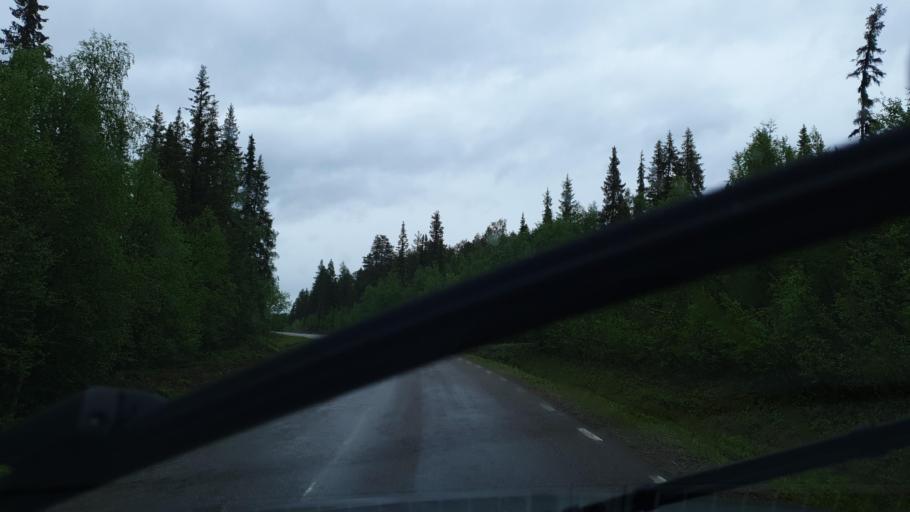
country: SE
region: Norrbotten
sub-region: Gallivare Kommun
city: Malmberget
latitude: 67.8900
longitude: 21.0409
